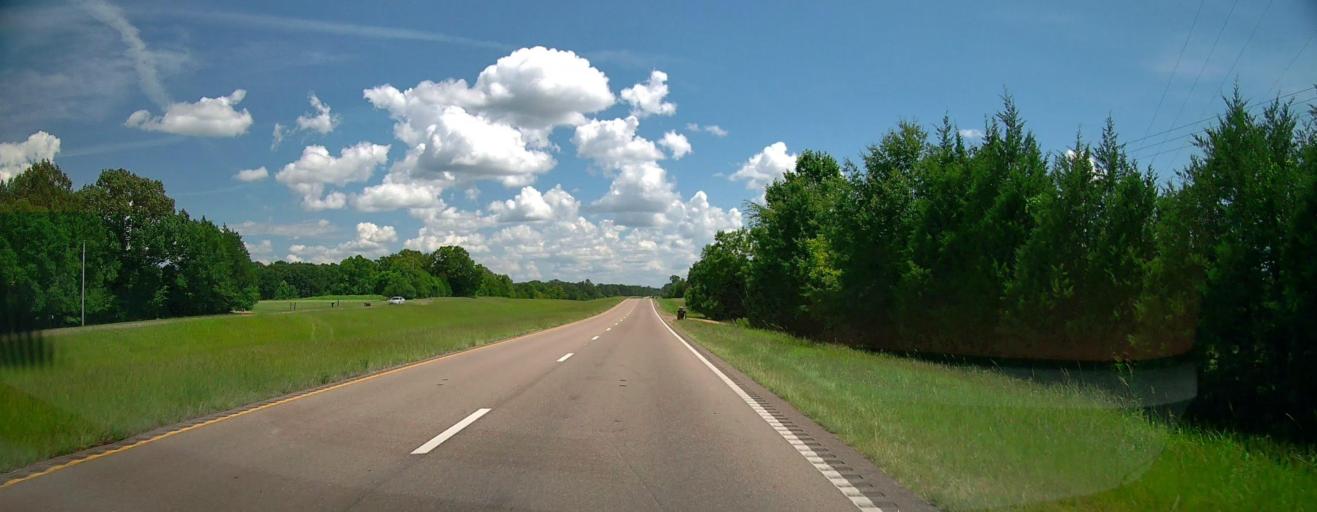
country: US
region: Mississippi
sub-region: Monroe County
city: Amory
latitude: 33.9516
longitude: -88.6038
